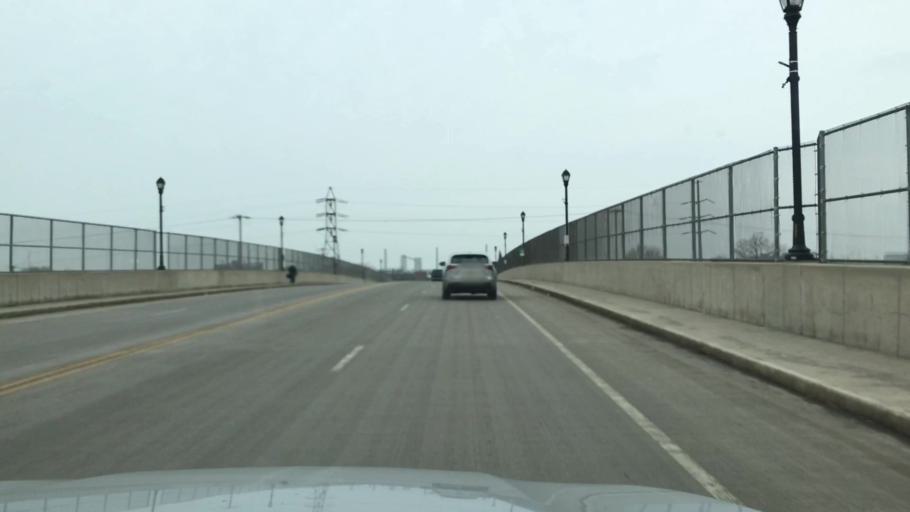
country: US
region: New York
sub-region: Erie County
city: Lackawanna
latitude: 42.8263
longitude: -78.8356
